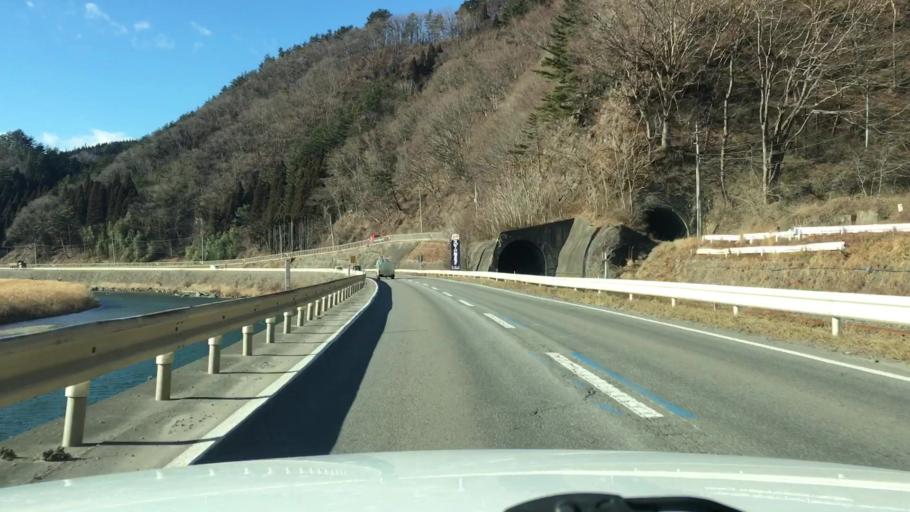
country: JP
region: Iwate
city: Miyako
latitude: 39.6351
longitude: 141.8481
